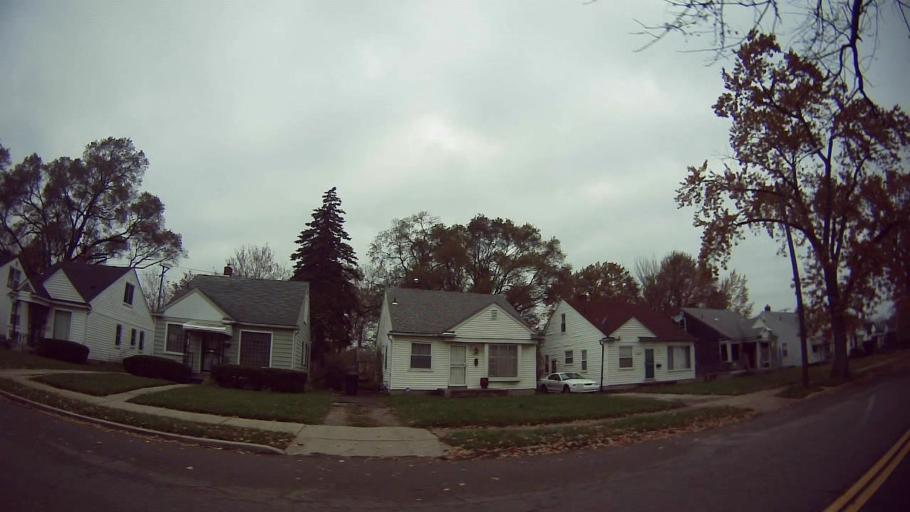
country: US
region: Michigan
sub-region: Oakland County
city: Hazel Park
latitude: 42.4410
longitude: -83.0831
